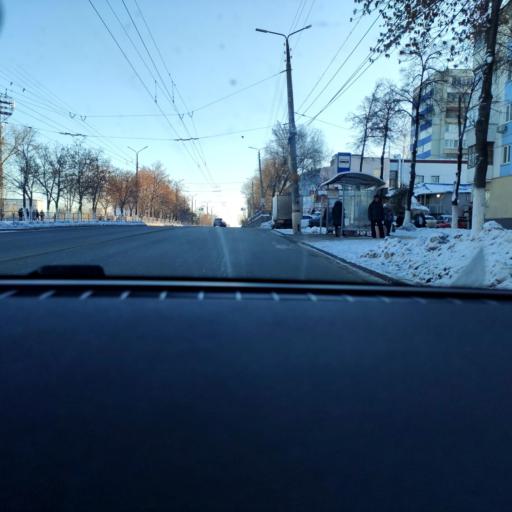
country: RU
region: Samara
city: Novokuybyshevsk
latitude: 53.1006
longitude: 49.9590
